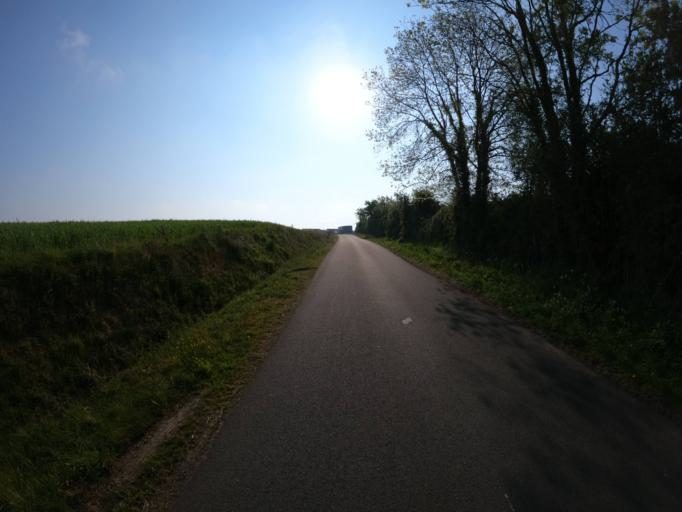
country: FR
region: Pays de la Loire
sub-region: Departement de Maine-et-Loire
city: La Seguiniere
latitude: 47.0676
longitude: -0.9570
